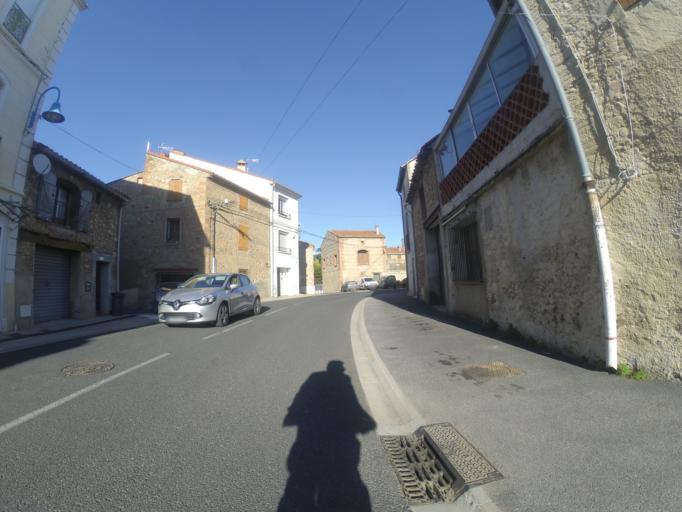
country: FR
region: Languedoc-Roussillon
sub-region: Departement des Pyrenees-Orientales
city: Corneilla-la-Riviere
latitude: 42.6800
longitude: 2.7390
